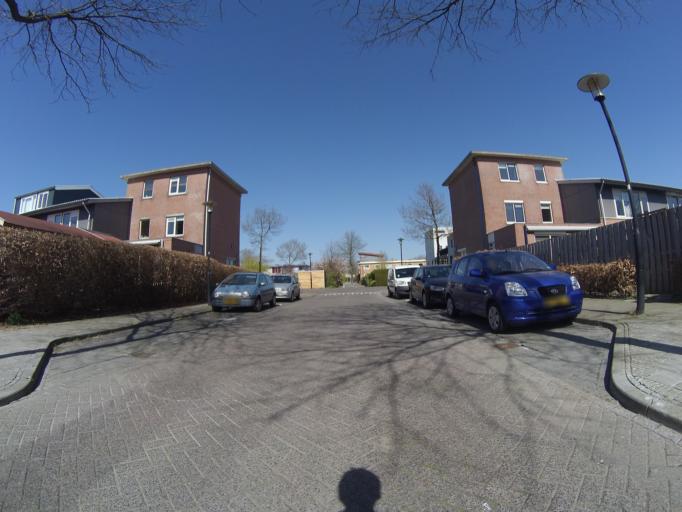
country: NL
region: Utrecht
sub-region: Gemeente Amersfoort
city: Hoogland
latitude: 52.1851
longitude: 5.3898
